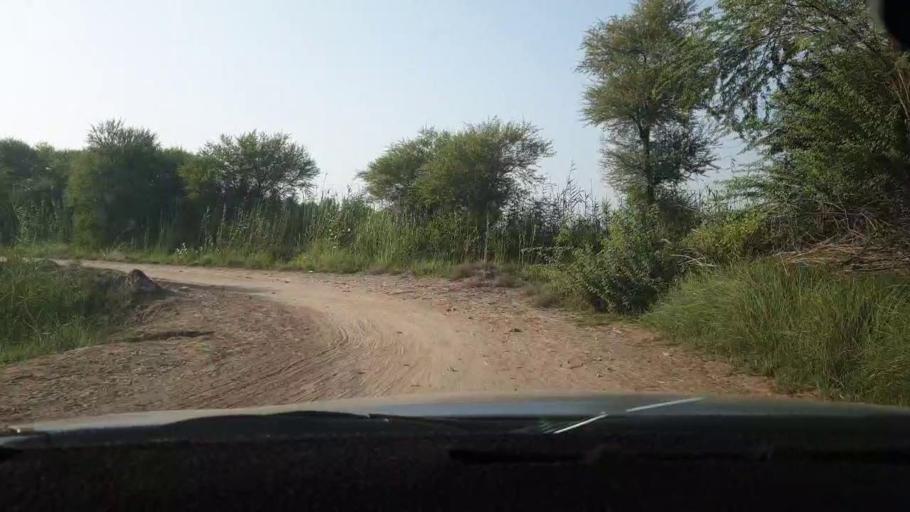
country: PK
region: Sindh
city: Pithoro
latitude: 25.6629
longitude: 69.4487
